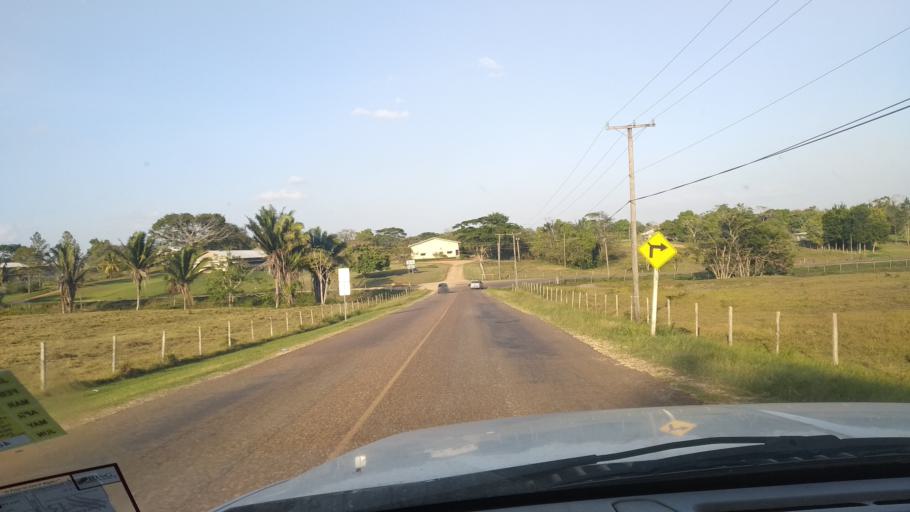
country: BZ
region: Cayo
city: San Ignacio
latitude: 17.2565
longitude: -88.9888
